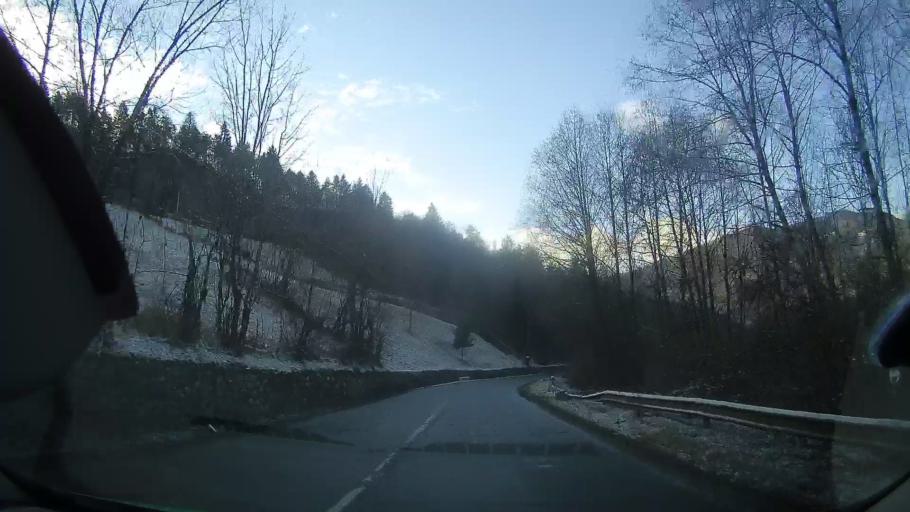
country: RO
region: Alba
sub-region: Comuna Sohodol
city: Sohodol
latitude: 46.3648
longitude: 23.0290
